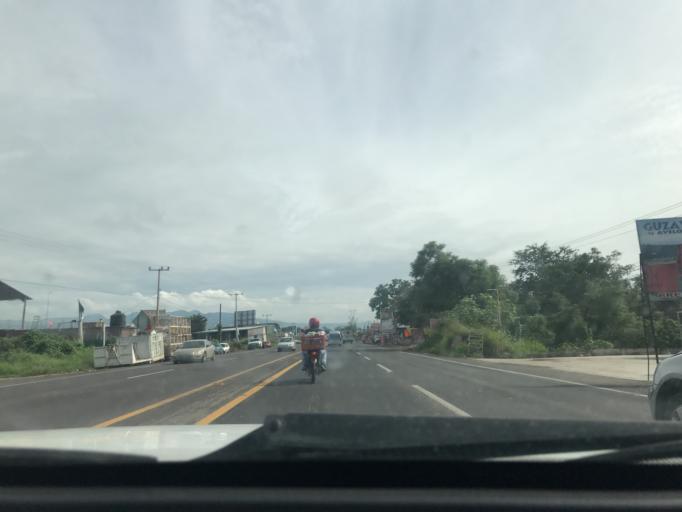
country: MX
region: Morelos
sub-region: Atlatlahucan
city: Colonia San Francisco
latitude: 18.8879
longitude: -98.9150
